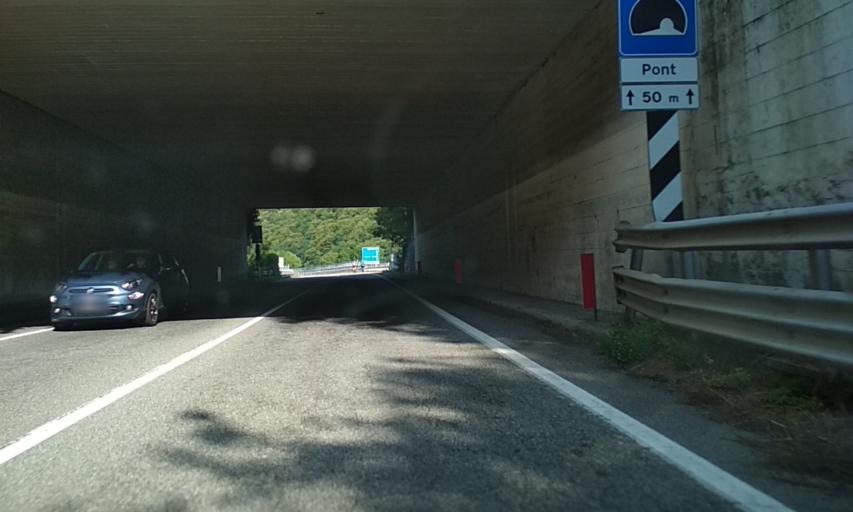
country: IT
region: Piedmont
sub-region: Provincia di Torino
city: Pont-Canavese
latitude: 45.4187
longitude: 7.5886
